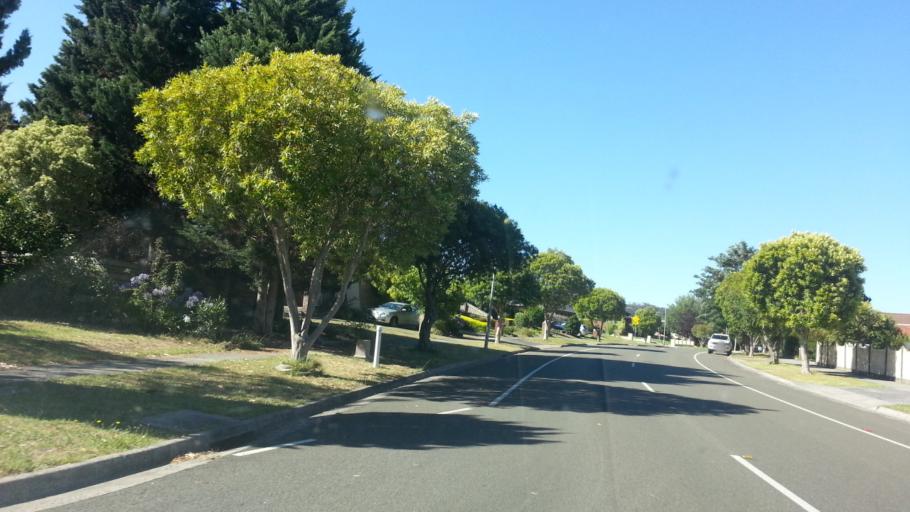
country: AU
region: Victoria
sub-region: Yarra Ranges
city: Lysterfield
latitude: -37.9223
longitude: 145.2686
